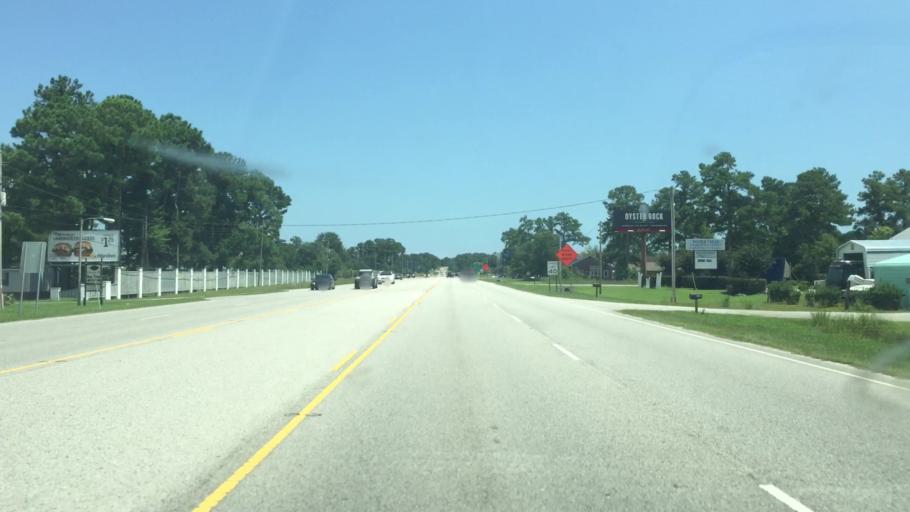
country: US
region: South Carolina
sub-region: Horry County
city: North Myrtle Beach
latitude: 33.8704
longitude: -78.6704
